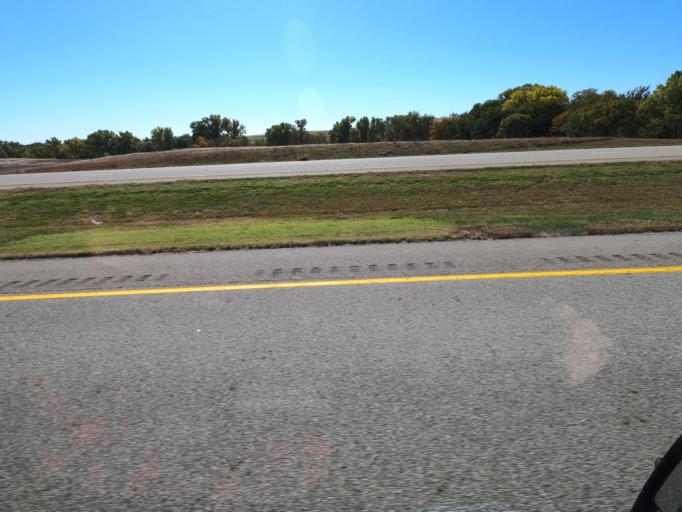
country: US
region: Kansas
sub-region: Russell County
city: Russell
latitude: 38.8629
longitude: -98.8338
